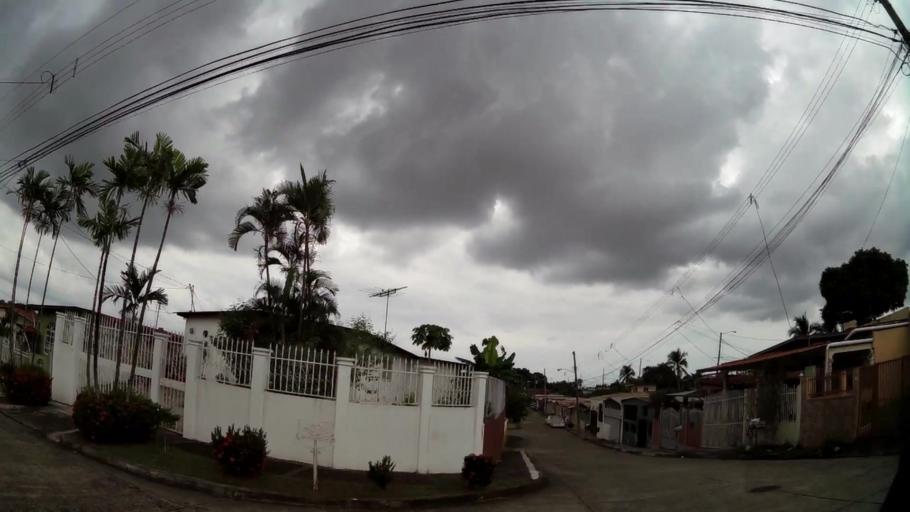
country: PA
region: Panama
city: Tocumen
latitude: 9.0604
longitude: -79.4174
